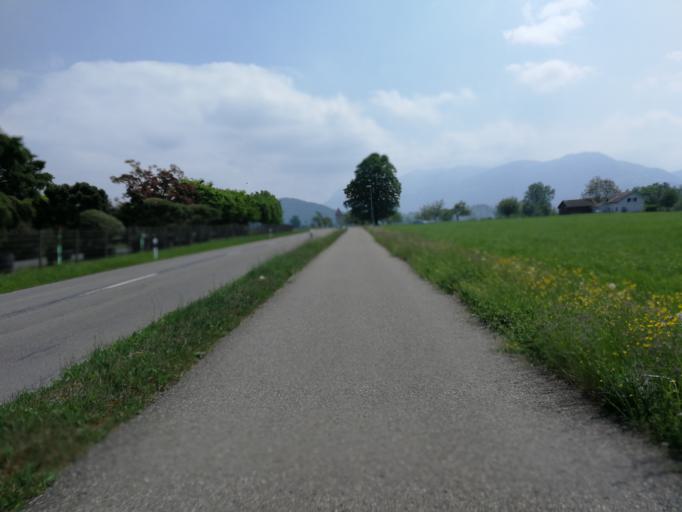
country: CH
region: Saint Gallen
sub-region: Wahlkreis See-Gaster
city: Jona
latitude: 47.2224
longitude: 8.8652
